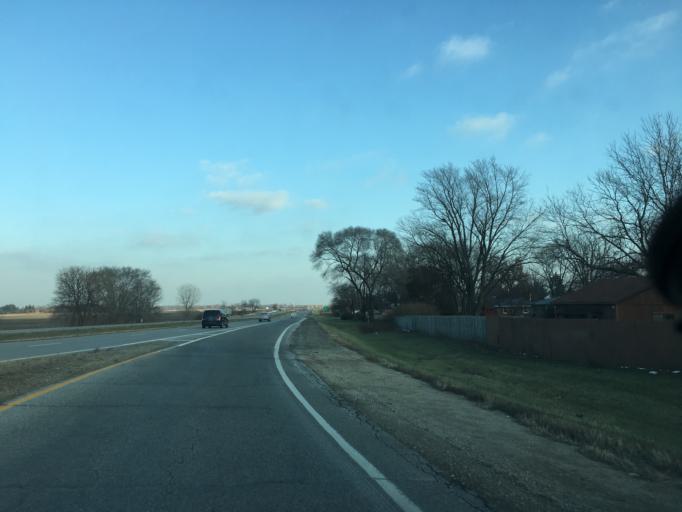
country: US
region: Illinois
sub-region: Kane County
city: Sugar Grove
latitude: 41.7651
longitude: -88.4387
